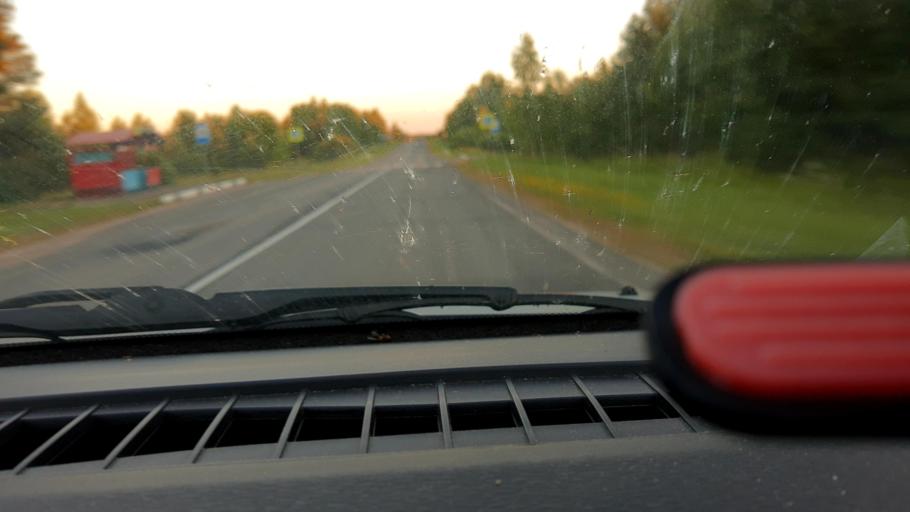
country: RU
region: Nizjnij Novgorod
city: Tonkino
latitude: 57.3215
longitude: 46.4734
